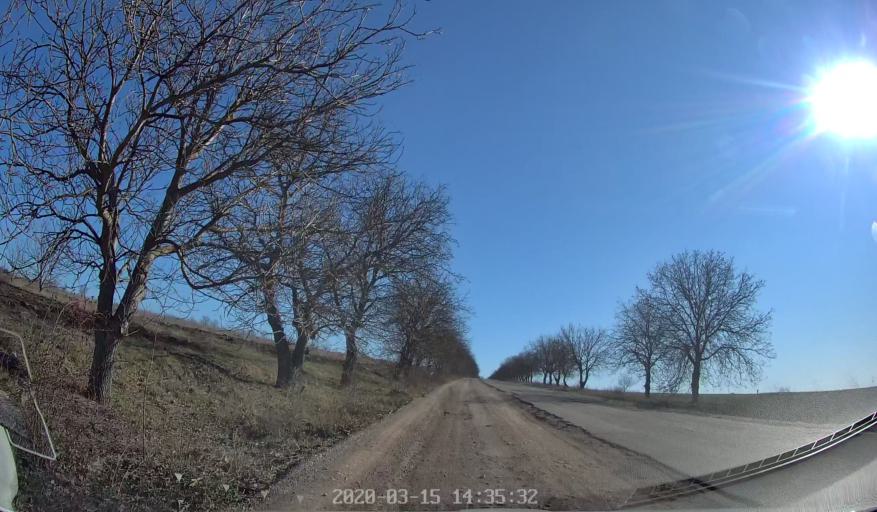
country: MD
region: Orhei
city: Orhei
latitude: 47.3290
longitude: 28.9248
